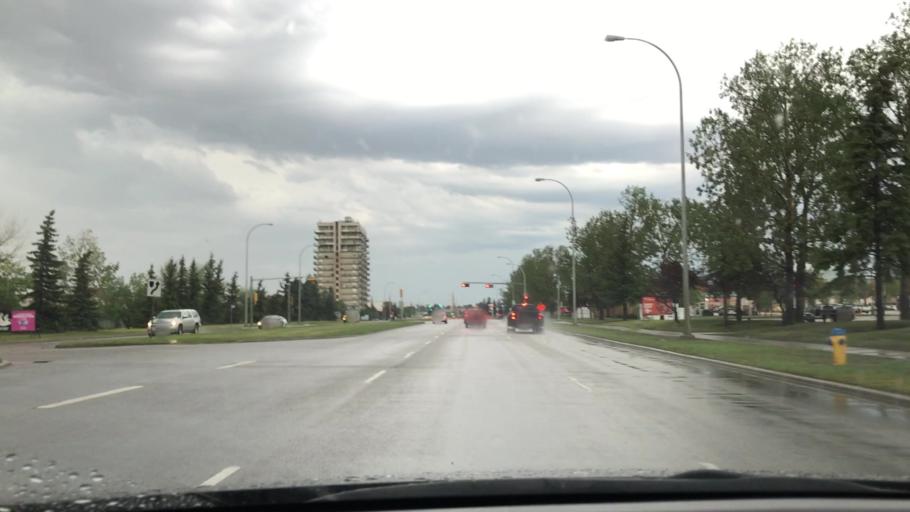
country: CA
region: Alberta
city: Edmonton
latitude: 53.4551
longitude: -113.4345
